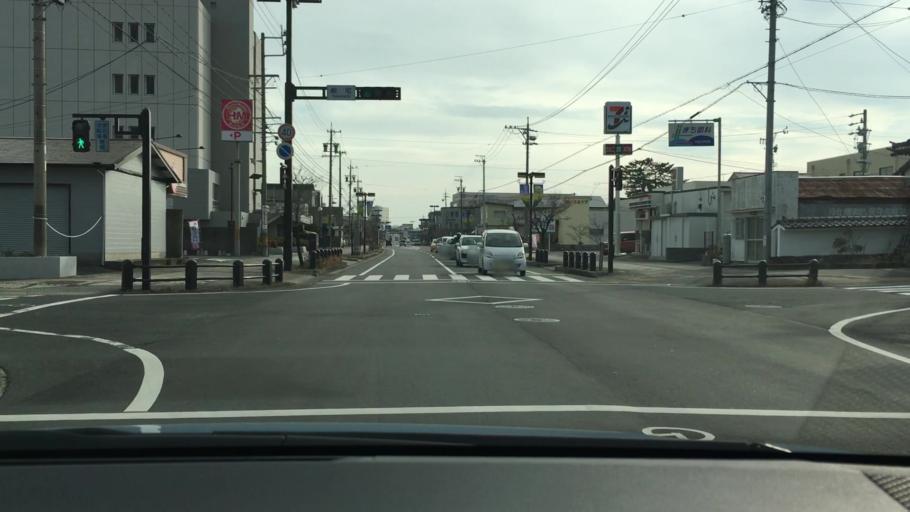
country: JP
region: Aichi
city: Tahara
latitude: 34.6729
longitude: 137.2707
